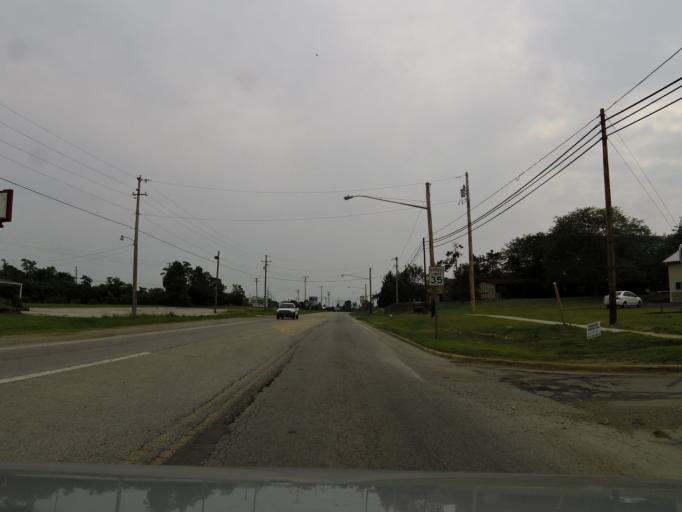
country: US
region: Ohio
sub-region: Clinton County
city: Wilmington
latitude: 39.4317
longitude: -83.8314
